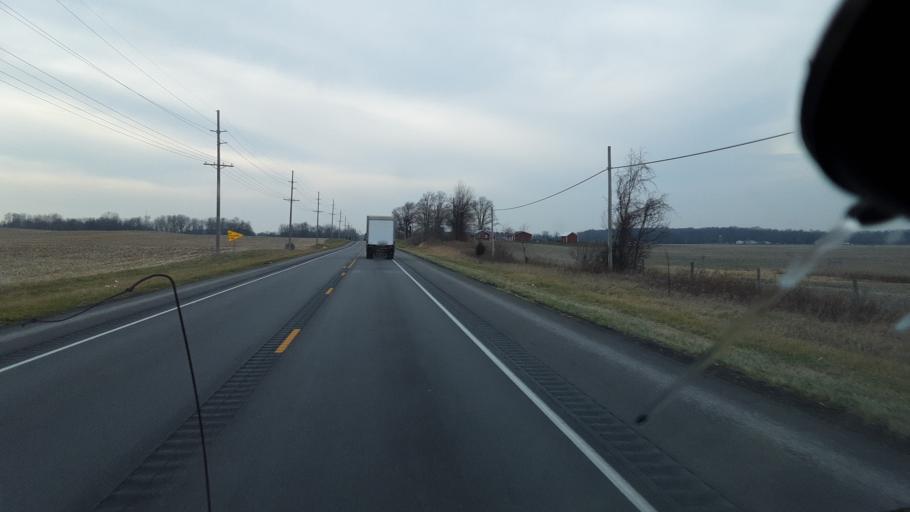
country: US
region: Indiana
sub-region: LaGrange County
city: Lagrange
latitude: 41.6417
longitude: -85.3734
